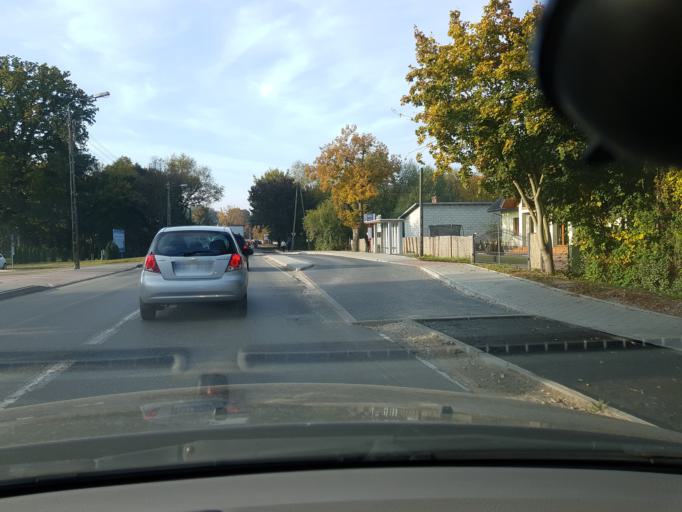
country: PL
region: Masovian Voivodeship
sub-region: Powiat otwocki
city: Jozefow
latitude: 52.1722
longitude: 21.2926
